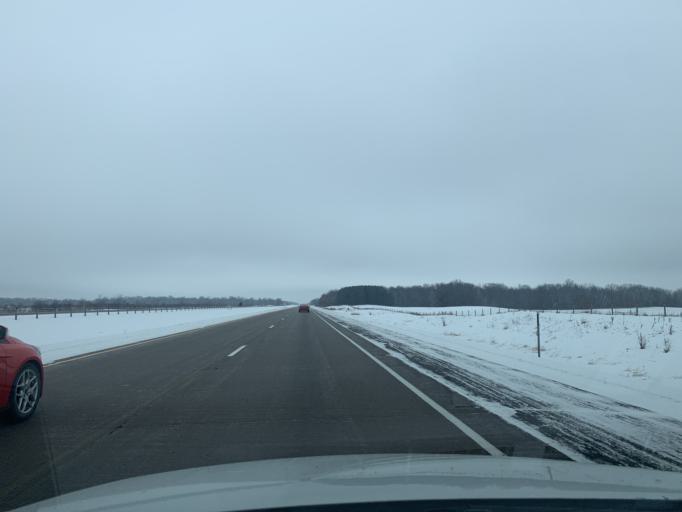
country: US
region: Minnesota
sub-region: Chisago County
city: Harris
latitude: 45.6224
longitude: -92.9921
